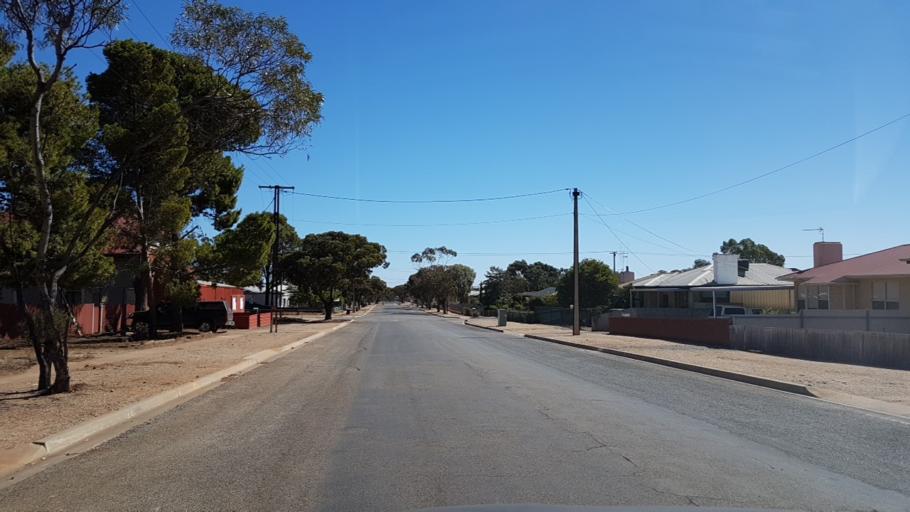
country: AU
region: South Australia
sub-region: Peterborough
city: Peterborough
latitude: -32.9789
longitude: 138.8269
